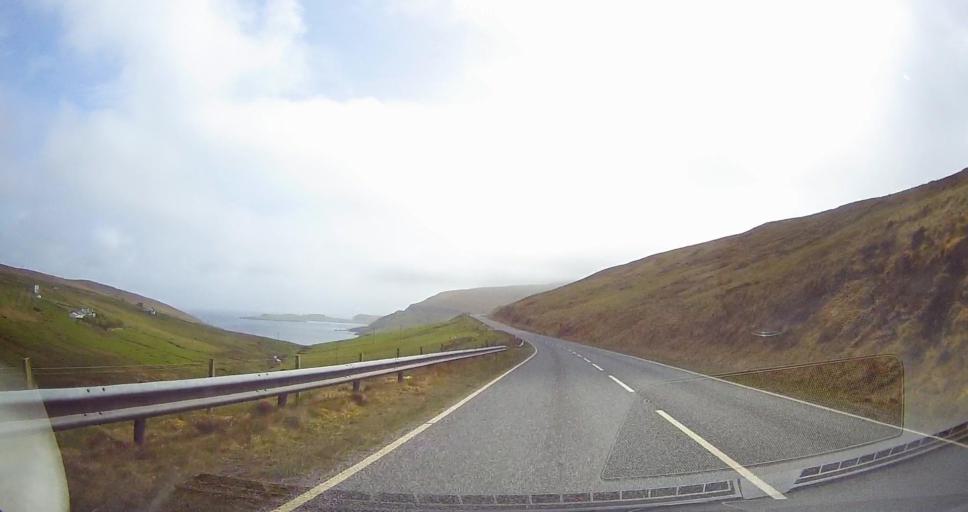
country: GB
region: Scotland
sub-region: Shetland Islands
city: Sandwick
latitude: 59.9992
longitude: -1.2795
